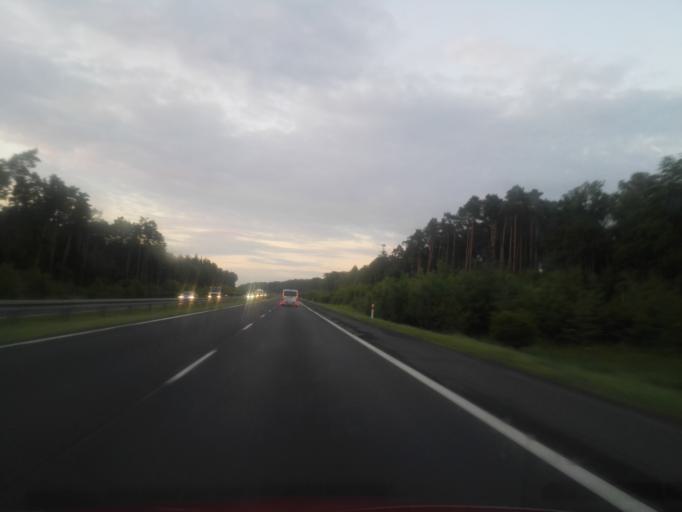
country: PL
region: Lodz Voivodeship
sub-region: Powiat radomszczanski
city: Gomunice
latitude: 51.1579
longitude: 19.4486
